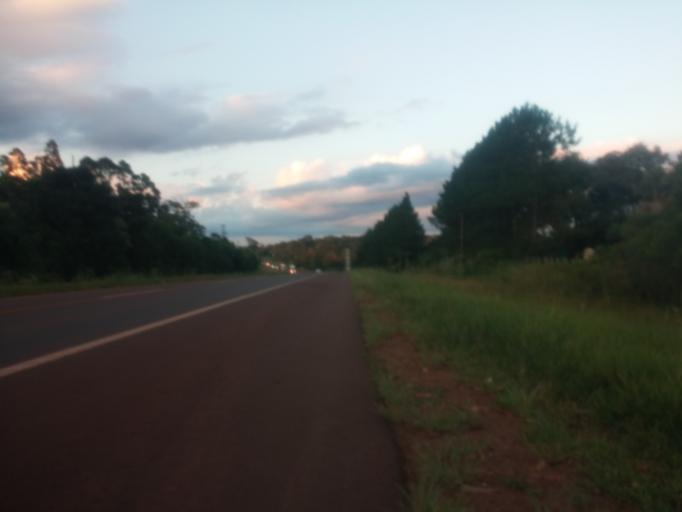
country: AR
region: Misiones
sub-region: Departamento de Obera
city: Obera
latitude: -27.4497
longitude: -55.0830
